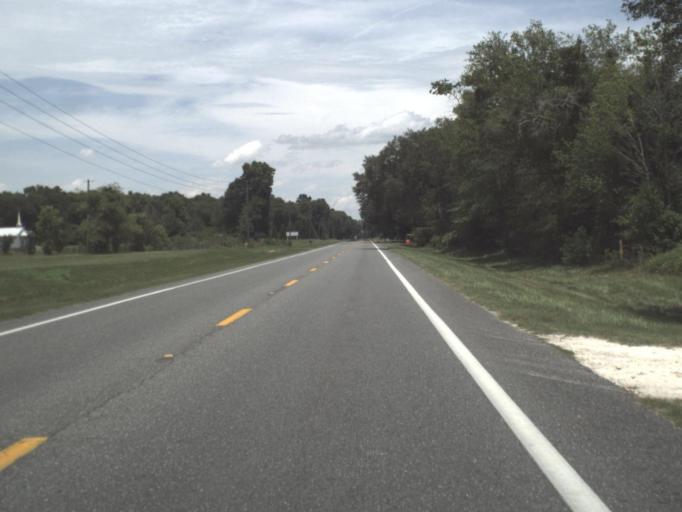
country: US
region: Florida
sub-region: Suwannee County
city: Live Oak
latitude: 30.2556
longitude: -83.0361
